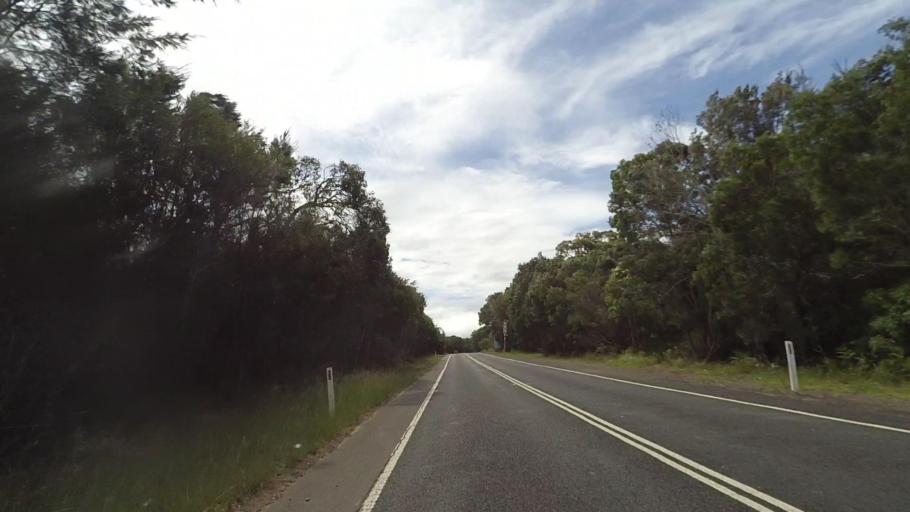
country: AU
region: New South Wales
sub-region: Sutherland Shire
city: Loftus
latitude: -34.0565
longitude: 151.0493
